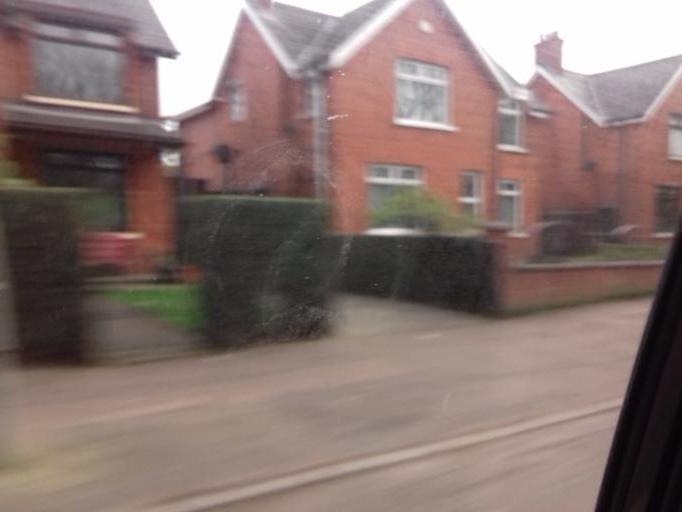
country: GB
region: Northern Ireland
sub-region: City of Belfast
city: Belfast
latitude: 54.6230
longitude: -5.9502
